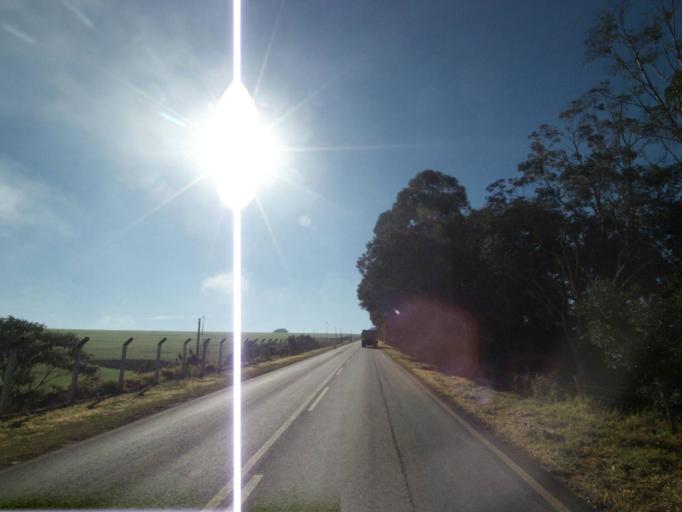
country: BR
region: Parana
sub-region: Tibagi
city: Tibagi
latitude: -24.5271
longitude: -50.3843
